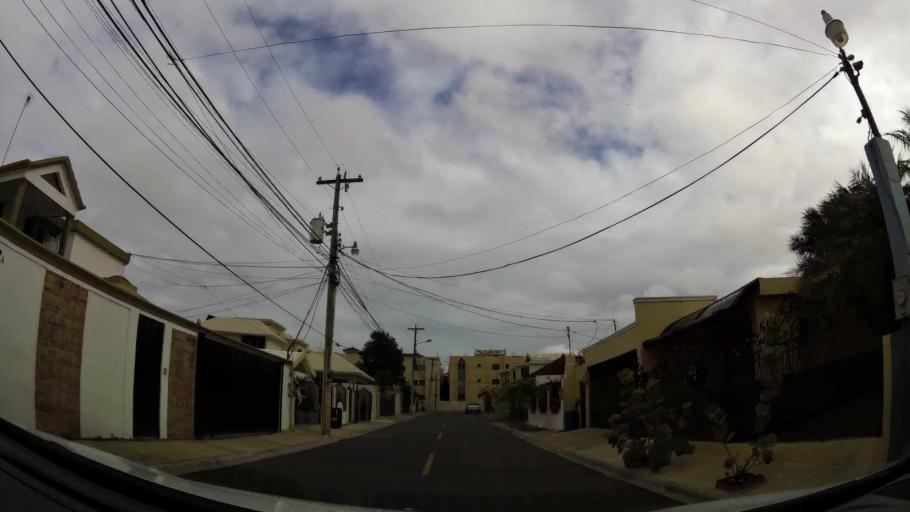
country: DO
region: Santiago
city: Santiago de los Caballeros
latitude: 19.4583
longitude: -70.6613
